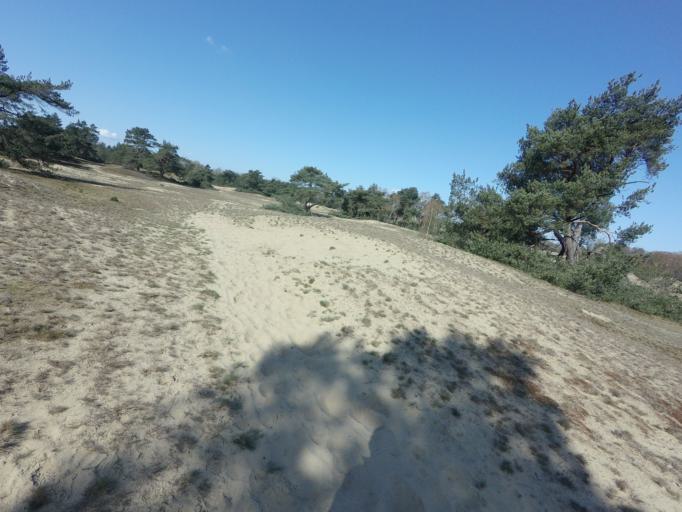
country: NL
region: Limburg
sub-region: Gemeente Bergen
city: Wellerlooi
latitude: 51.5999
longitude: 6.0715
